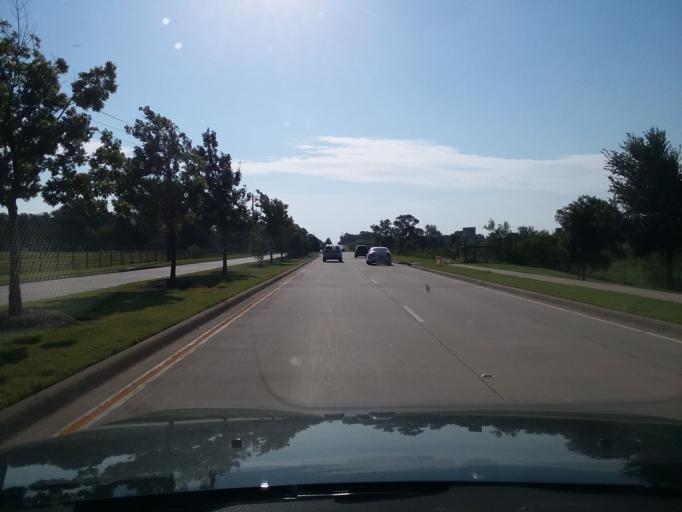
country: US
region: Texas
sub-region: Denton County
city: Double Oak
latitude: 33.0664
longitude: -97.0766
